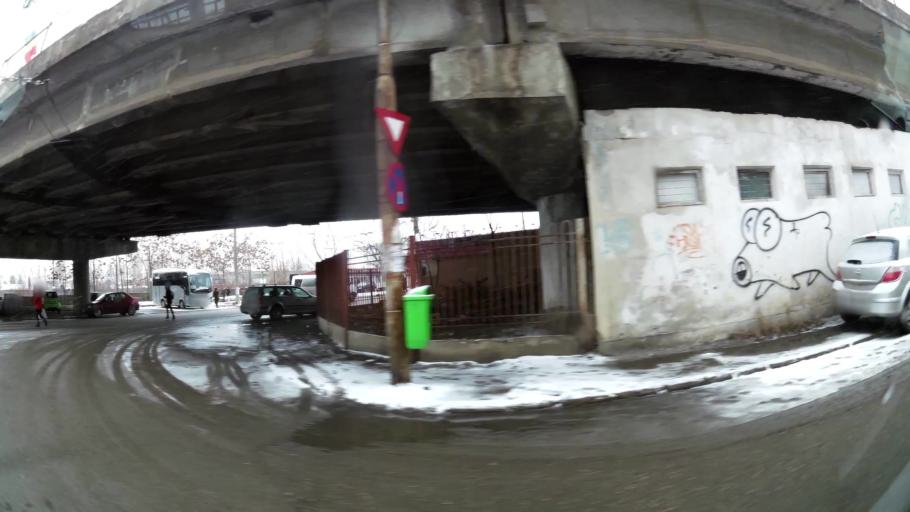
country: RO
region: Dambovita
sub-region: Municipiul Targoviste
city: Targoviste
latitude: 44.9178
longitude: 25.4524
